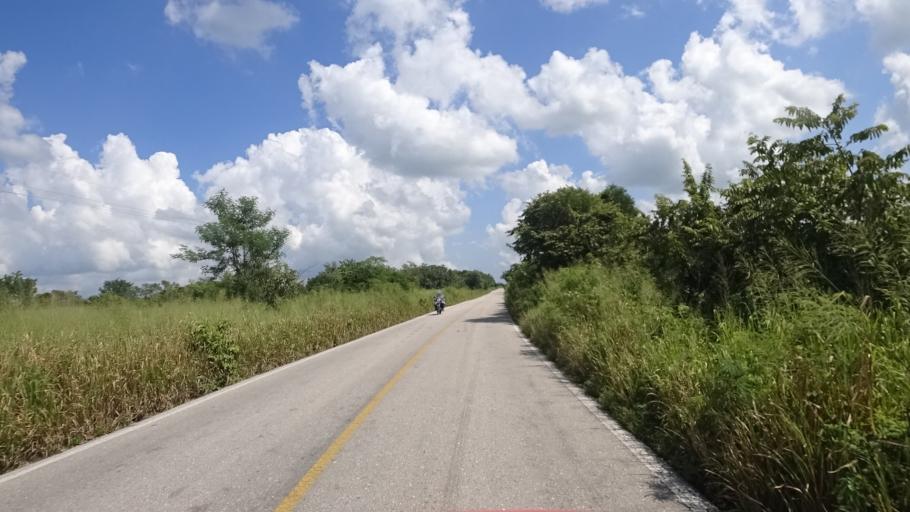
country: MX
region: Yucatan
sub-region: Panaba
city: Loche
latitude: 21.4426
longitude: -88.1397
